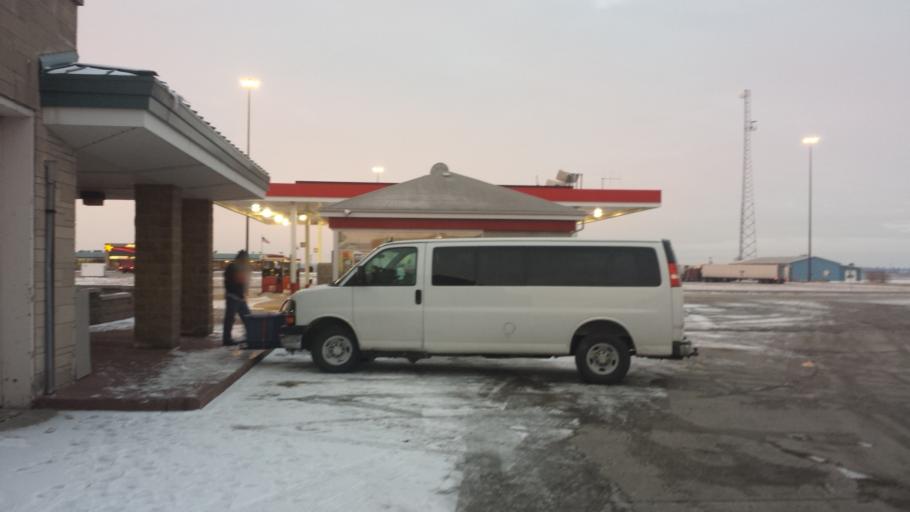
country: US
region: Michigan
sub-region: Saint Joseph County
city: Sturgis
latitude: 41.7468
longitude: -85.3286
